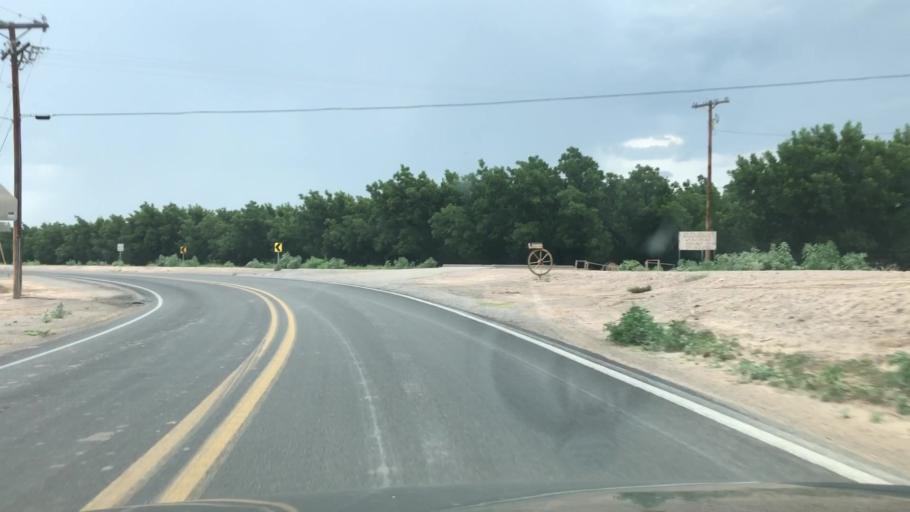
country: US
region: New Mexico
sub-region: Dona Ana County
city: La Union
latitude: 31.9858
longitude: -106.6496
